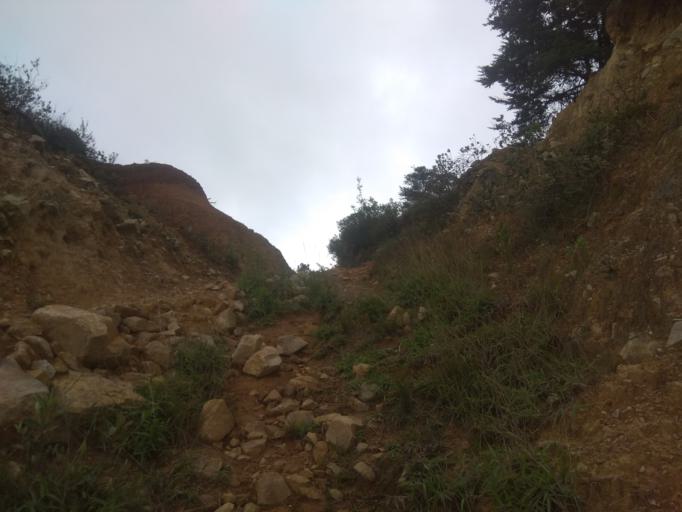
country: CO
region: Boyaca
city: Socha Viejo
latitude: 6.0076
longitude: -72.6788
